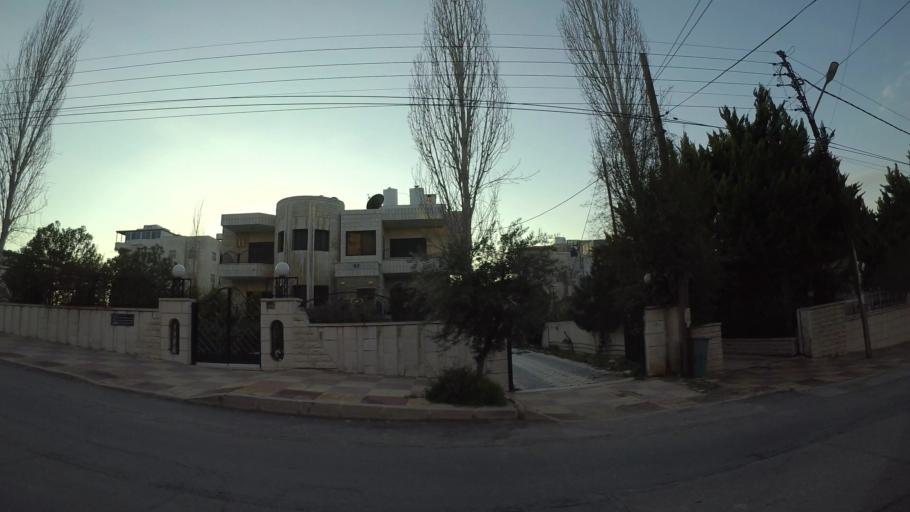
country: JO
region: Amman
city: Al Jubayhah
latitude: 31.9962
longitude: 35.8749
